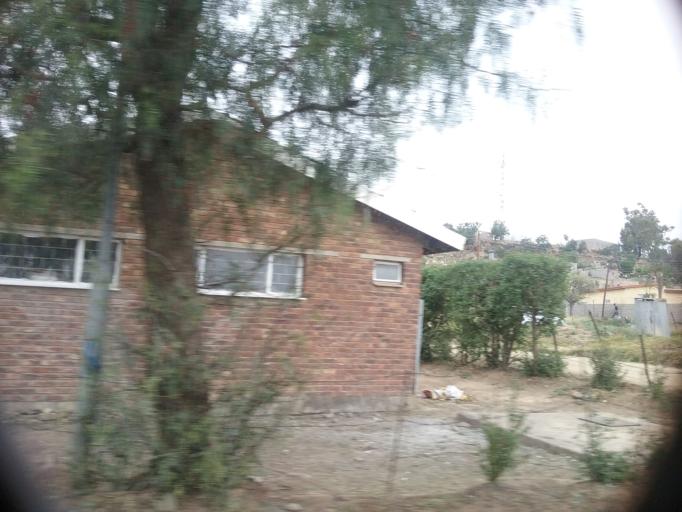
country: LS
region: Maseru
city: Maseru
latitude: -29.3200
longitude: 27.5104
